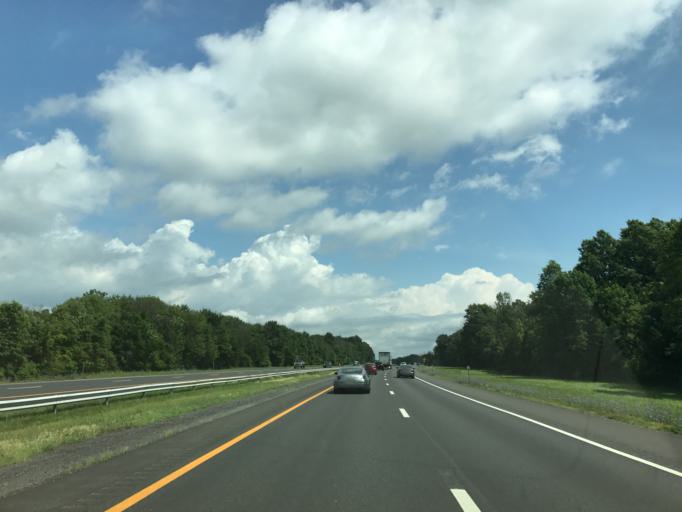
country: US
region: New York
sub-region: Ulster County
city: Saugerties
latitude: 42.1273
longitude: -73.9548
